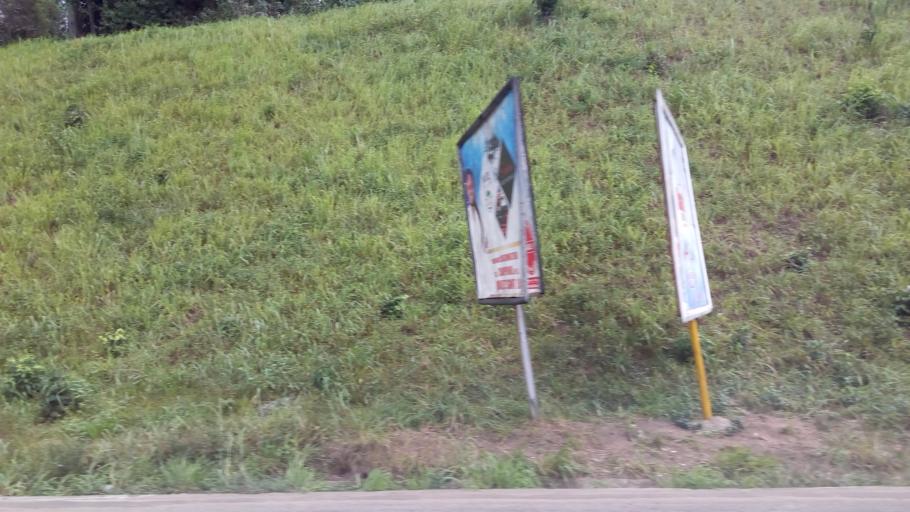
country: CI
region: Lagunes
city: Abidjan
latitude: 5.3583
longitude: -4.0556
